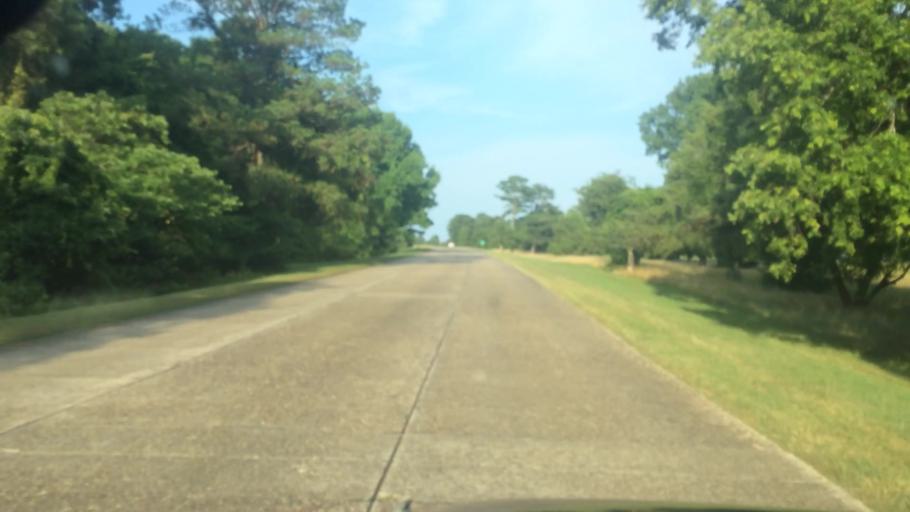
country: US
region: Virginia
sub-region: James City County
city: Williamsburg
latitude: 37.2134
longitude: -76.7325
